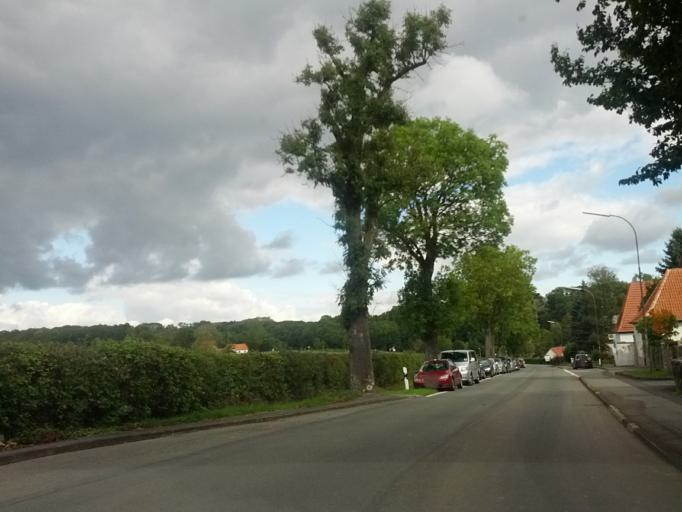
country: DE
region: Hesse
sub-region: Regierungsbezirk Kassel
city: Herleshausen
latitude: 51.0513
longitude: 10.1181
